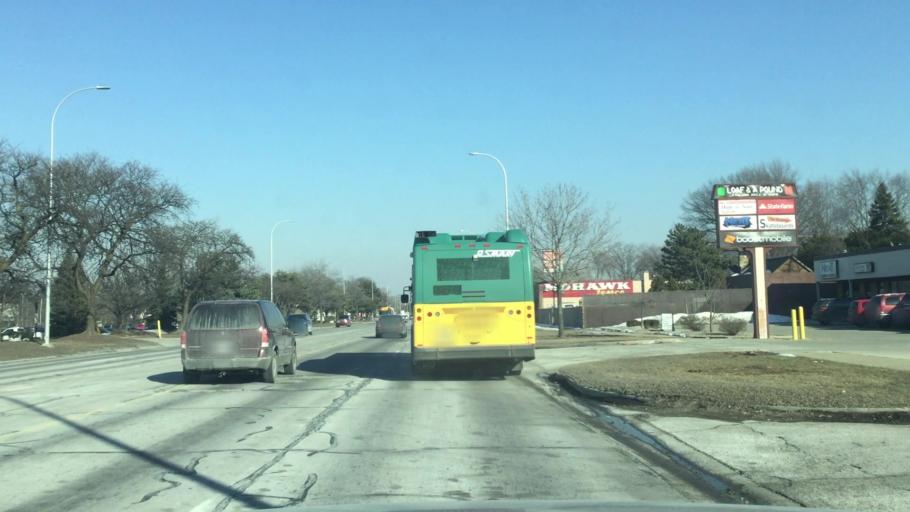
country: US
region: Michigan
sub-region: Wayne County
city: Westland
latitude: 42.3245
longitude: -83.3838
